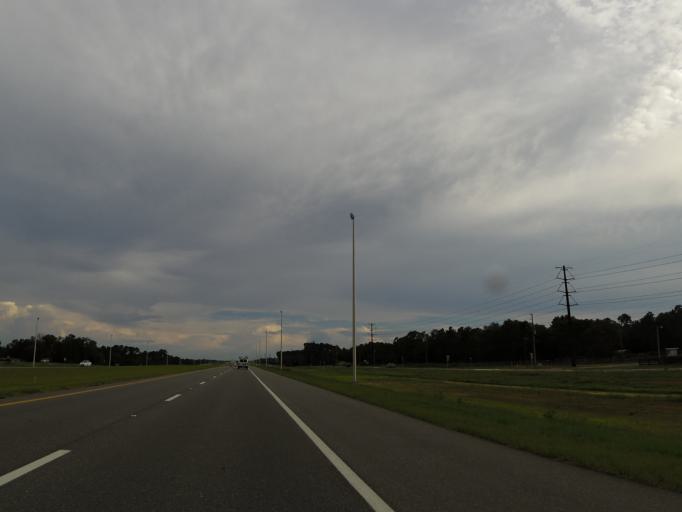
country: US
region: Florida
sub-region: Clay County
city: Lakeside
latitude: 30.1490
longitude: -81.8311
